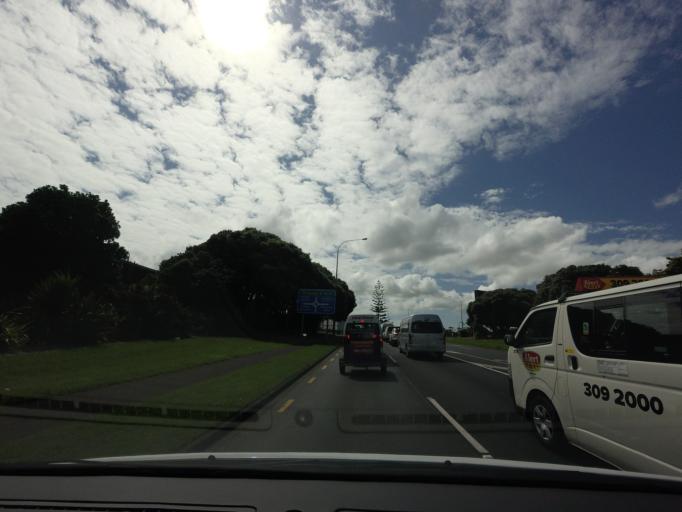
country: NZ
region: Auckland
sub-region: Auckland
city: Mangere
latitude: -36.9994
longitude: 174.7879
